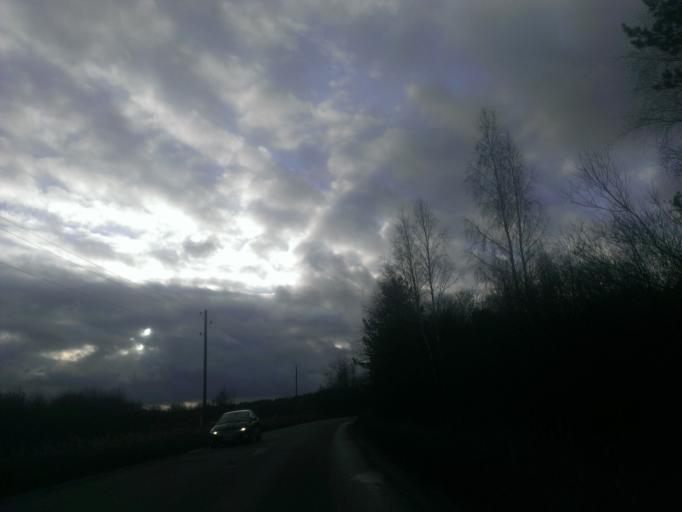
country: LV
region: Riga
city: Bolderaja
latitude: 57.0663
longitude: 24.0867
